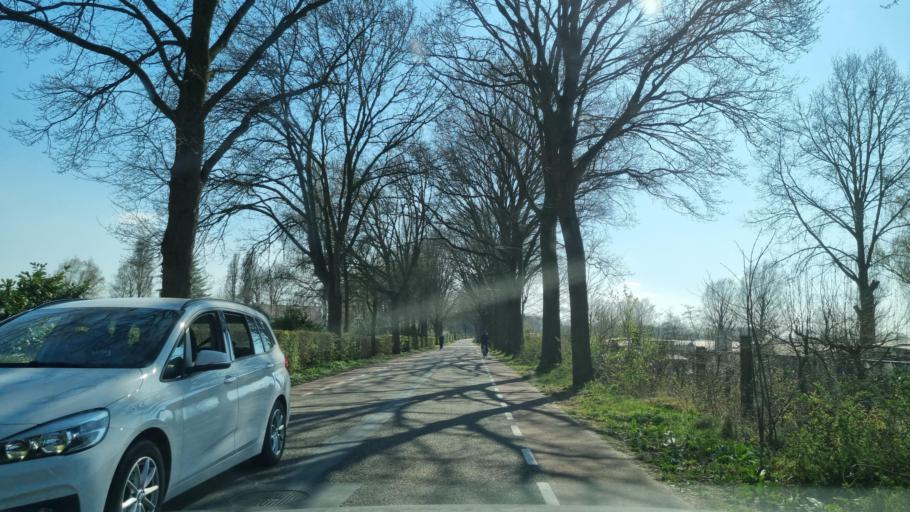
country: NL
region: Gelderland
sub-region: Gemeente Groesbeek
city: Bredeweg
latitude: 51.7353
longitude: 5.9174
